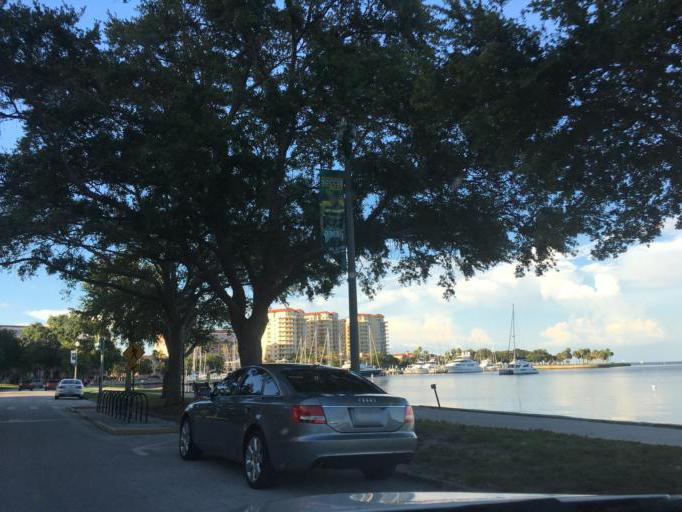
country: US
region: Florida
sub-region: Pinellas County
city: Saint Petersburg
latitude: 27.7753
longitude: -82.6311
